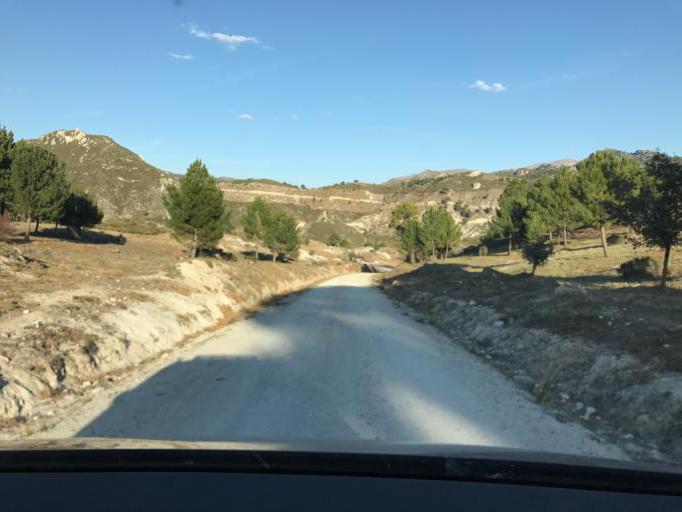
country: ES
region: Andalusia
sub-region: Provincia de Granada
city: Quentar
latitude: 37.2338
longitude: -3.4127
